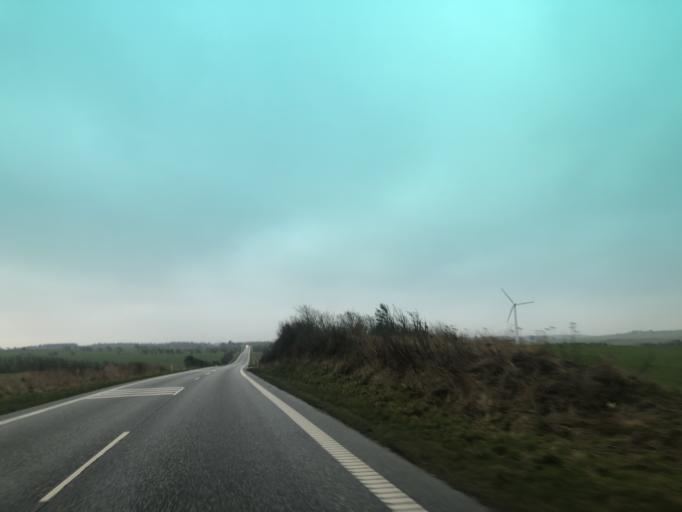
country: DK
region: North Denmark
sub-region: Thisted Kommune
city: Hurup
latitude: 56.7026
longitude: 8.4100
